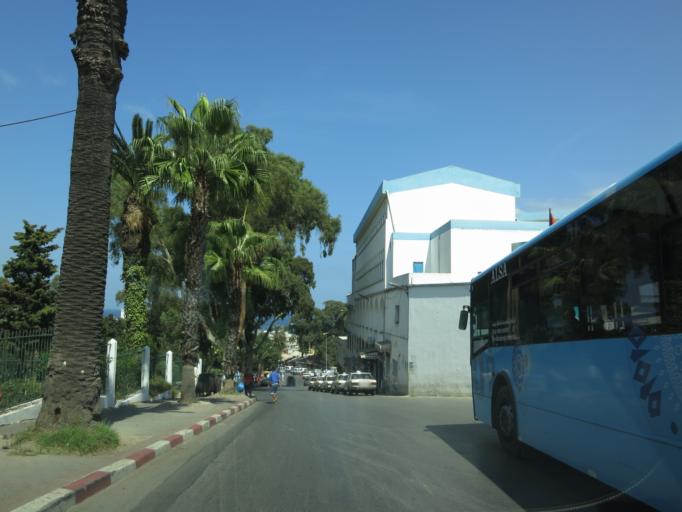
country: MA
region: Tanger-Tetouan
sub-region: Tanger-Assilah
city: Tangier
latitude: 35.7822
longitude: -5.8156
